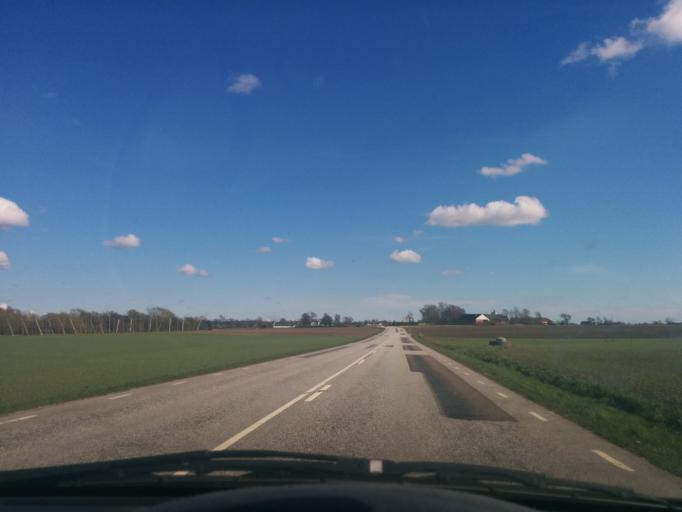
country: SE
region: Skane
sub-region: Svedala Kommun
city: Klagerup
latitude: 55.6360
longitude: 13.2817
